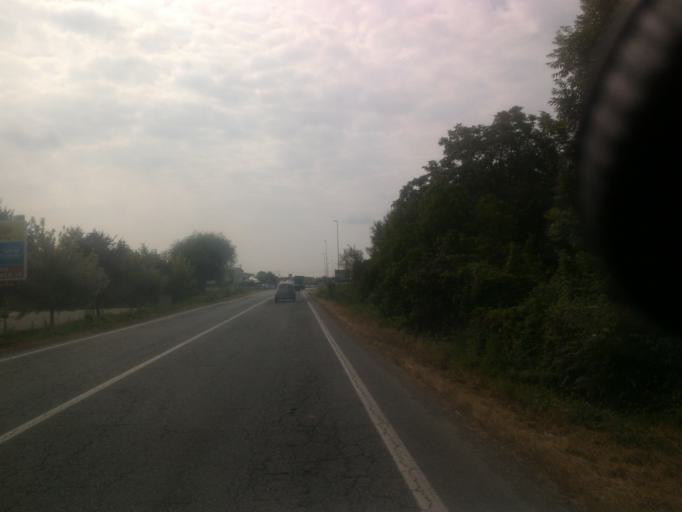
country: IT
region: Piedmont
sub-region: Provincia di Torino
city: Bricherasio
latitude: 44.8307
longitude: 7.3088
